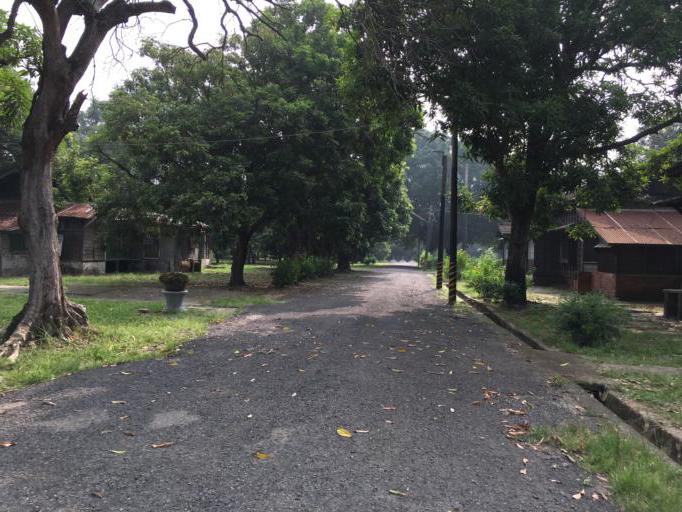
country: TW
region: Taiwan
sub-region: Chiayi
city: Taibao
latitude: 23.4816
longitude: 120.2977
